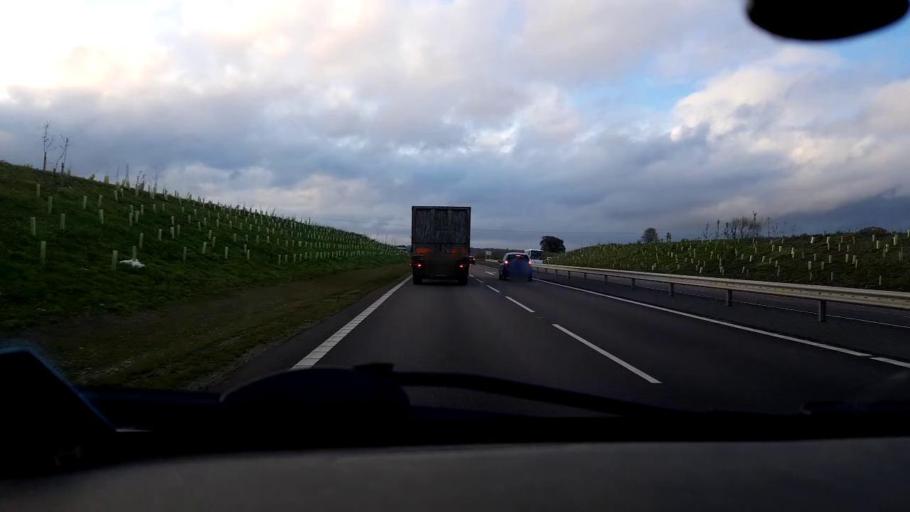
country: GB
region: England
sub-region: Norfolk
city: Horsford
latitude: 52.6853
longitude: 1.2446
